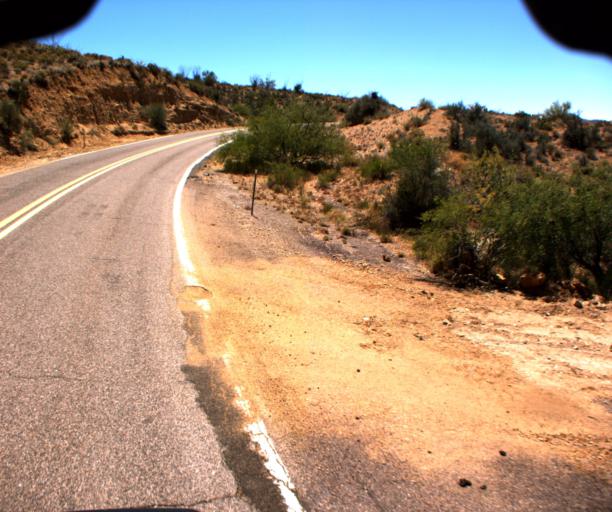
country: US
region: Arizona
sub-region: Yavapai County
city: Bagdad
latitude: 34.4601
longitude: -112.9975
